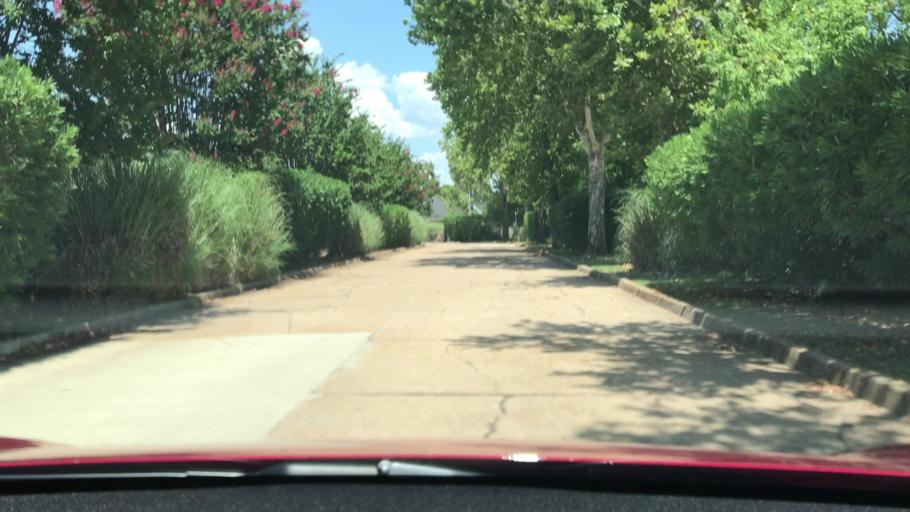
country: US
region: Louisiana
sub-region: Bossier Parish
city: Bossier City
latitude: 32.4269
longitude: -93.7196
